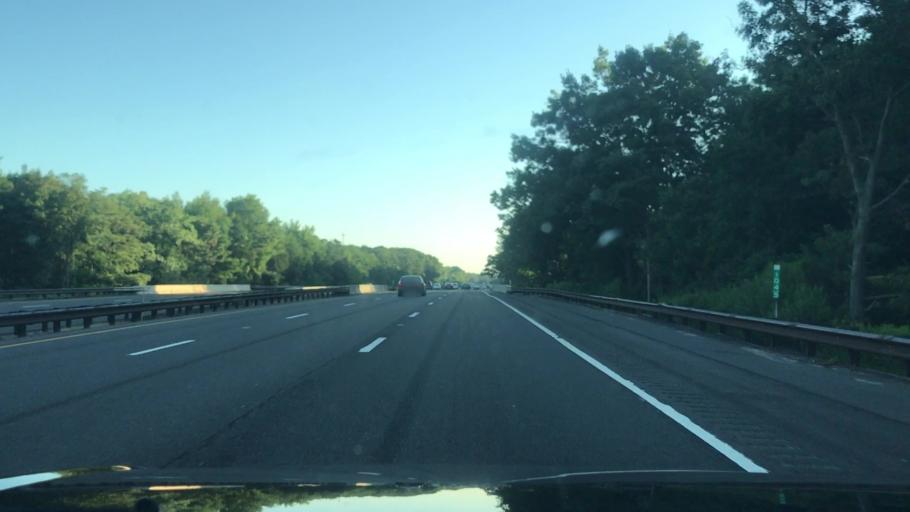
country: US
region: New Jersey
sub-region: Monmouth County
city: Eatontown
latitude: 40.2580
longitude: -74.0795
